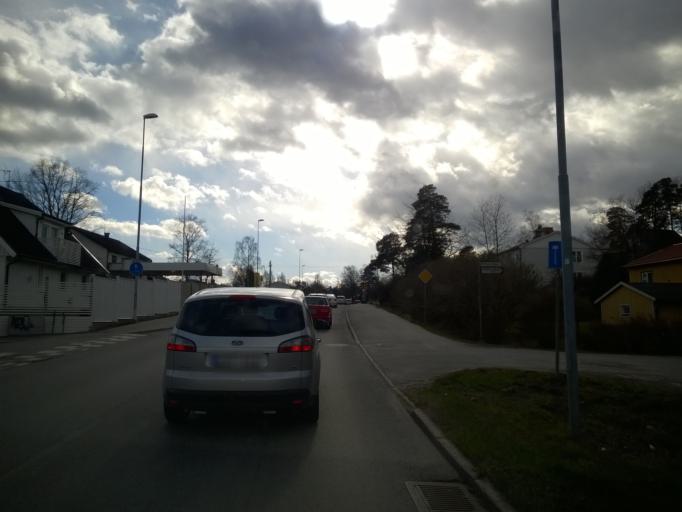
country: SE
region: Stockholm
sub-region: Jarfalla Kommun
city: Jakobsberg
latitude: 59.3869
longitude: 17.8375
